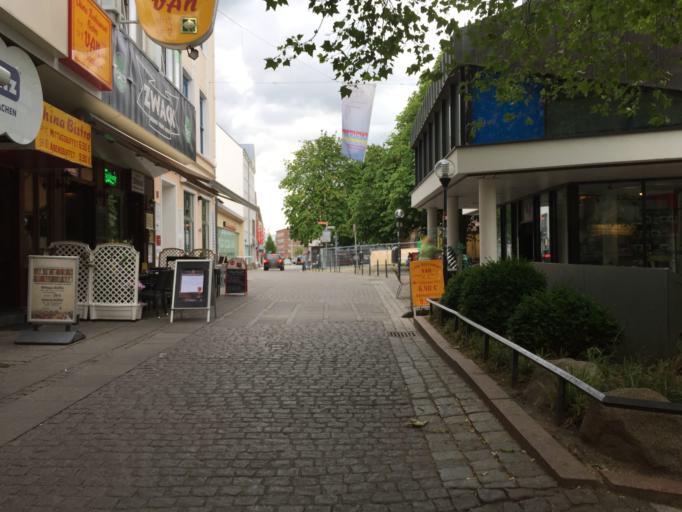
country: DE
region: Schleswig-Holstein
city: Kiel
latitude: 54.3236
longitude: 10.1396
